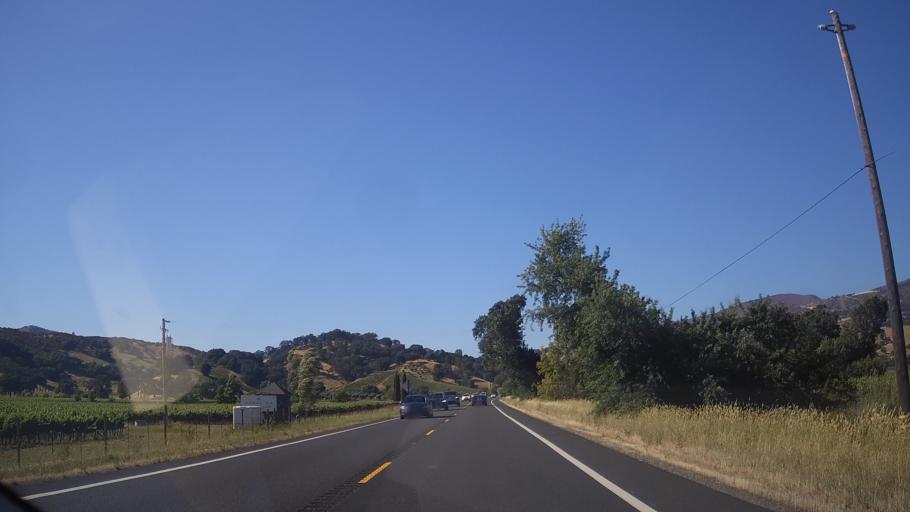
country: US
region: California
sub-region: Mendocino County
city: Talmage
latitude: 38.9898
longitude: -123.1186
